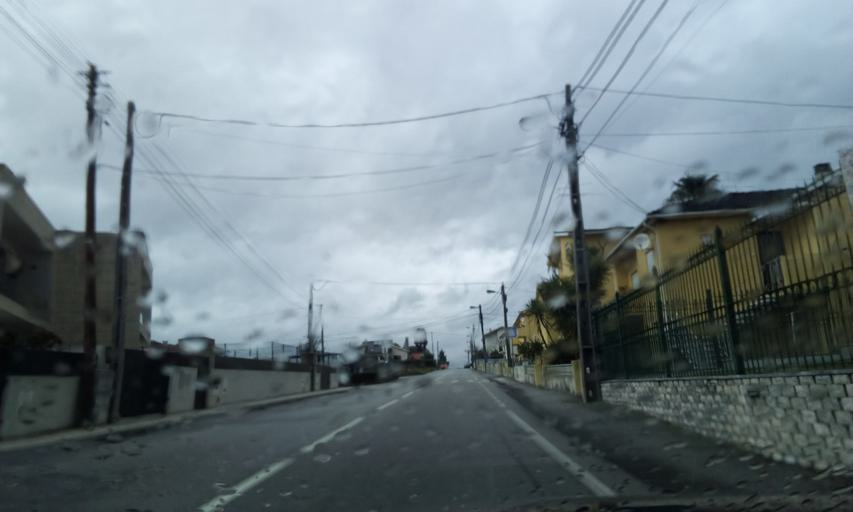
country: PT
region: Viseu
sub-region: Viseu
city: Rio de Loba
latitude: 40.6359
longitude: -7.8664
